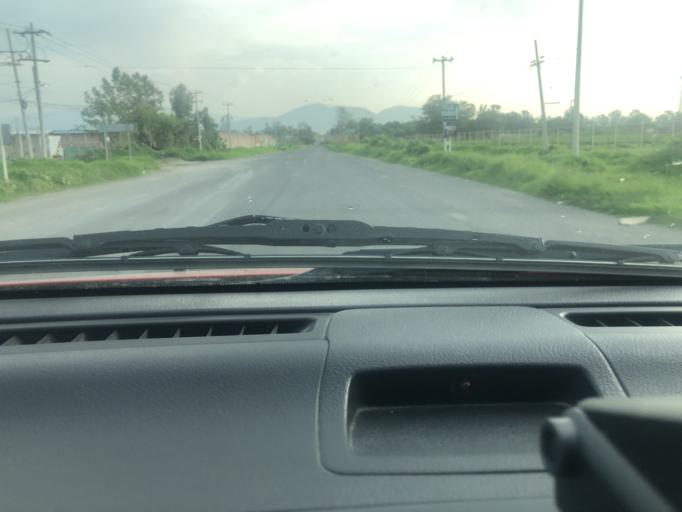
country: MX
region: Jalisco
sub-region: San Pedro Tlaquepaque
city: Paseo del Prado
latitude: 20.5742
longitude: -103.4052
